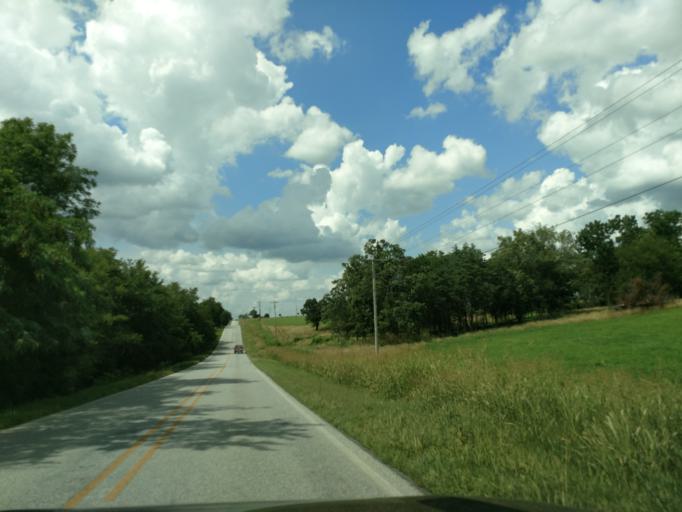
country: US
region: Arkansas
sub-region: Carroll County
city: Berryville
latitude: 36.4623
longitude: -93.5558
